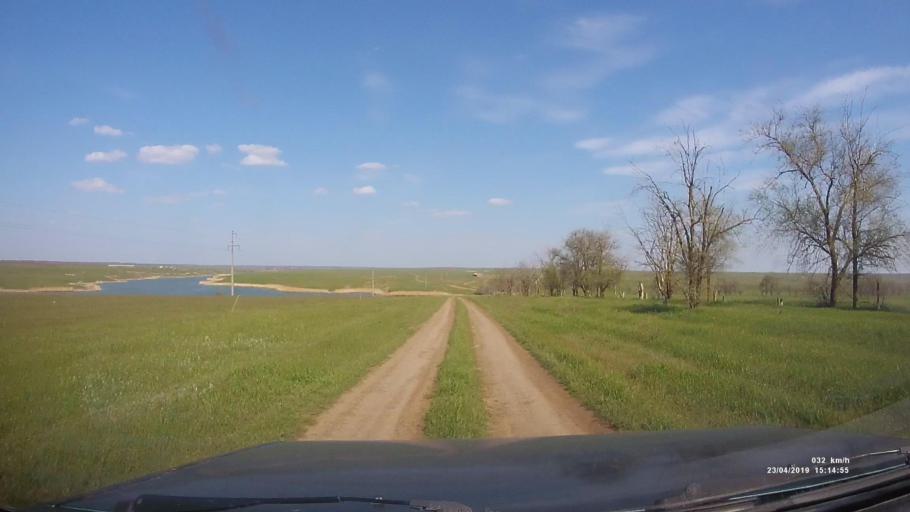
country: RU
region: Rostov
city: Remontnoye
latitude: 46.5397
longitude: 42.9666
